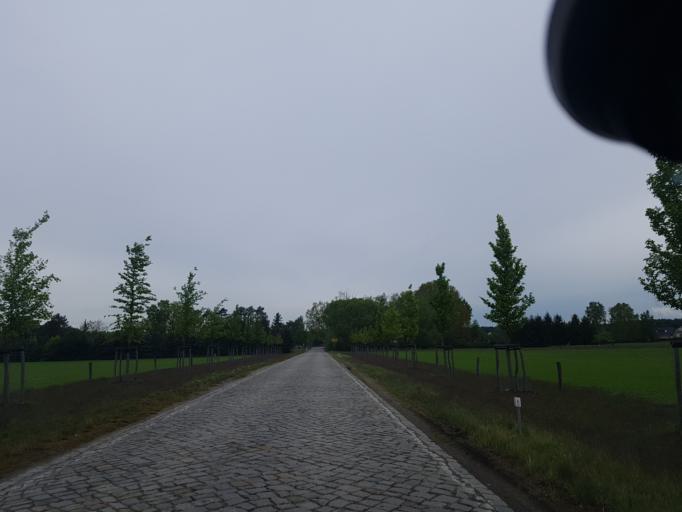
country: DE
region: Brandenburg
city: Spremberg
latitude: 51.6516
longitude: 14.4312
